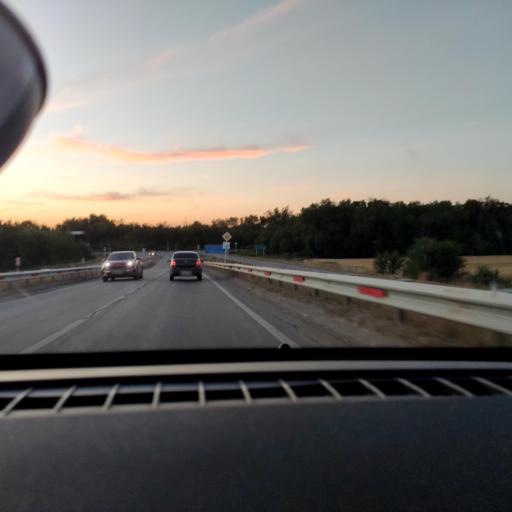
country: RU
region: Samara
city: Kinel'
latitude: 53.2644
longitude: 50.5436
